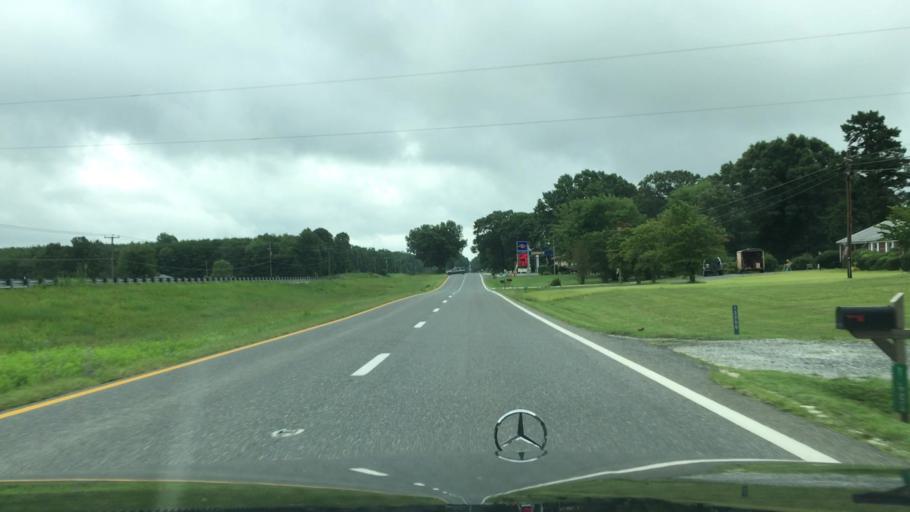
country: US
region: Virginia
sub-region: Appomattox County
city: Appomattox
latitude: 37.3249
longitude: -78.7739
